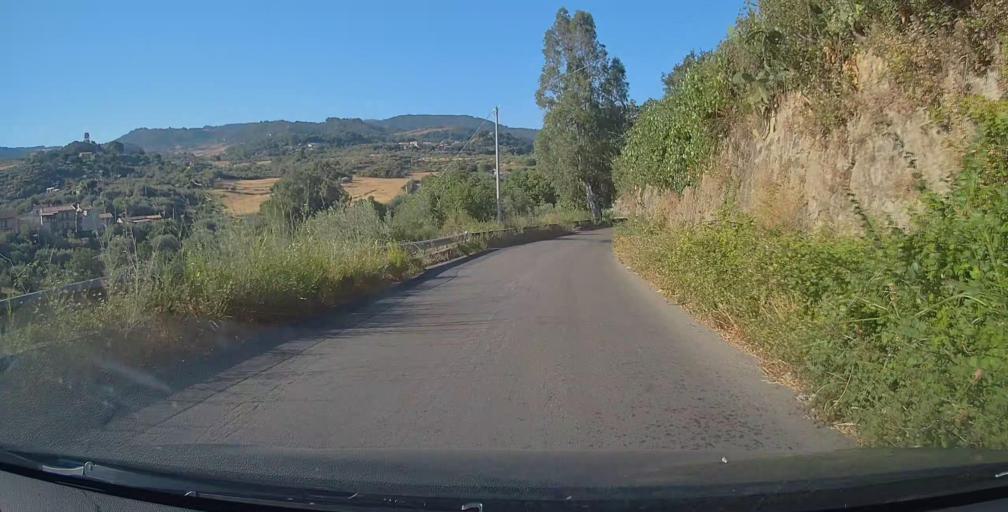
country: IT
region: Sicily
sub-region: Messina
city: Librizzi
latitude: 38.0793
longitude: 14.9726
